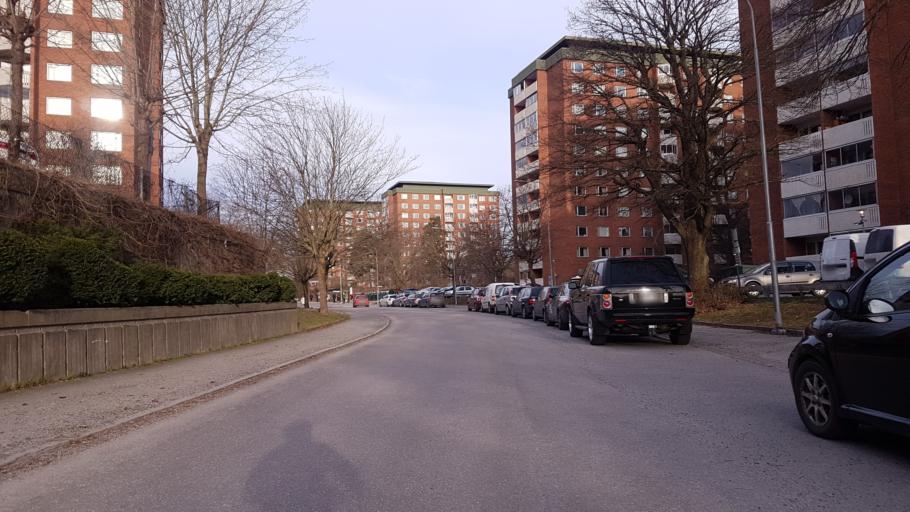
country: SE
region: Stockholm
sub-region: Lidingo
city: Lidingoe
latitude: 59.3459
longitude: 18.1491
